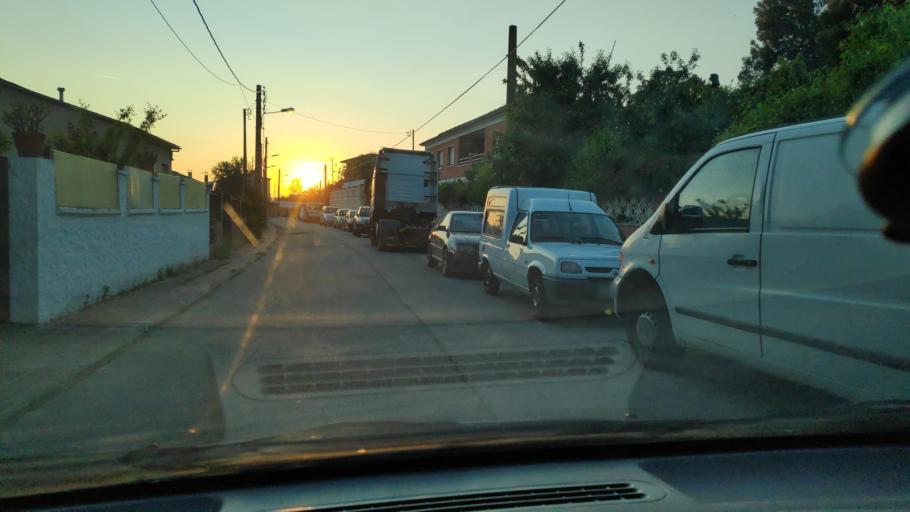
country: ES
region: Catalonia
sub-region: Provincia de Barcelona
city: Sant Quirze del Valles
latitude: 41.5318
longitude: 2.0509
